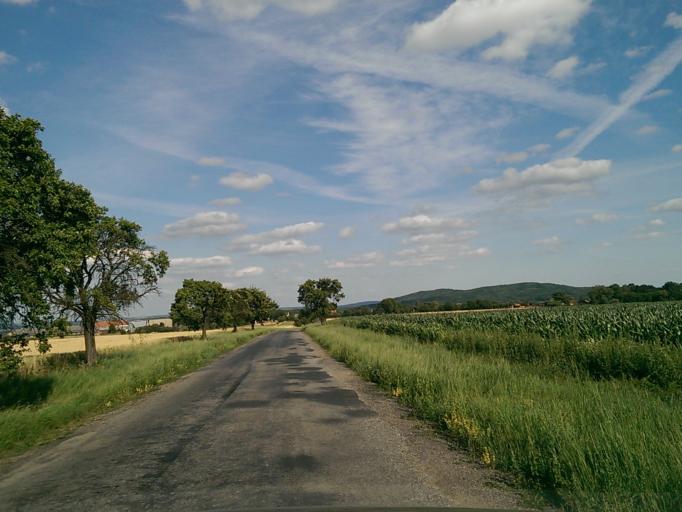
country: CZ
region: Central Bohemia
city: Bakov nad Jizerou
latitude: 50.4777
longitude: 14.8994
